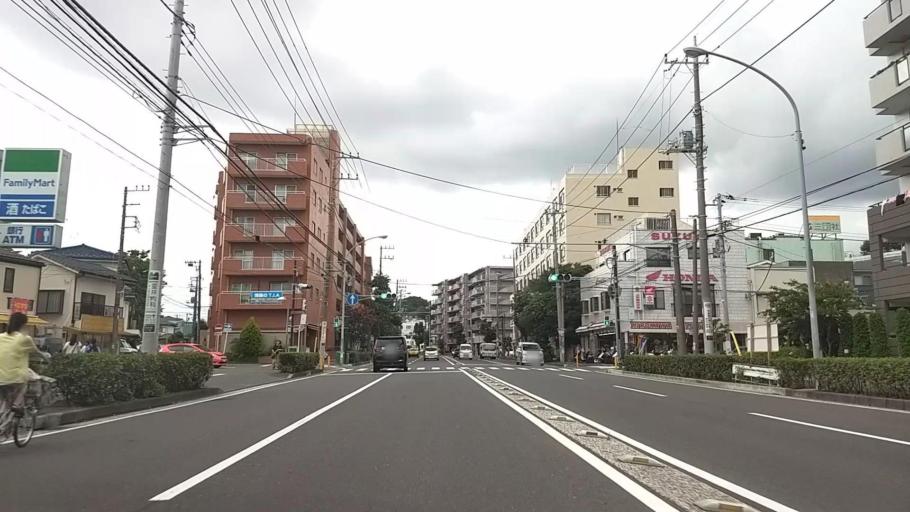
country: JP
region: Kanagawa
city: Yokohama
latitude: 35.4365
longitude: 139.5990
